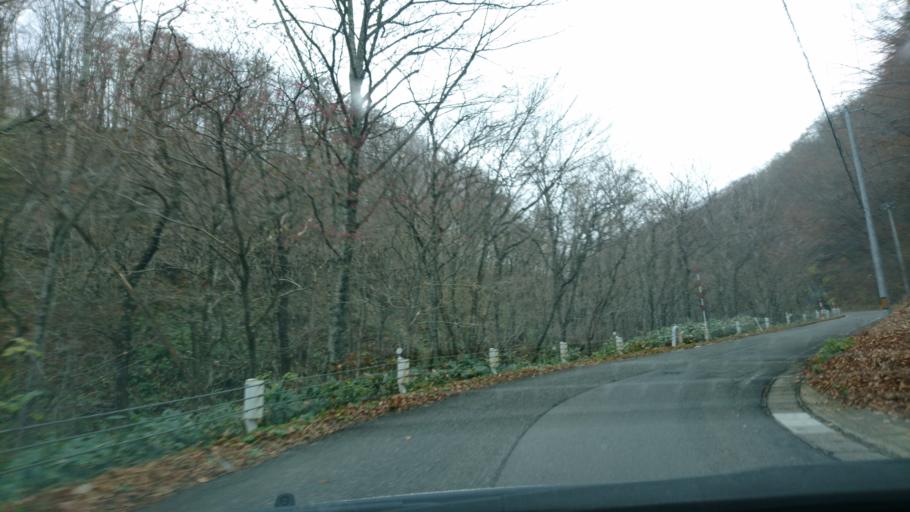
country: JP
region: Iwate
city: Ichinoseki
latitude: 38.9109
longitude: 140.8549
